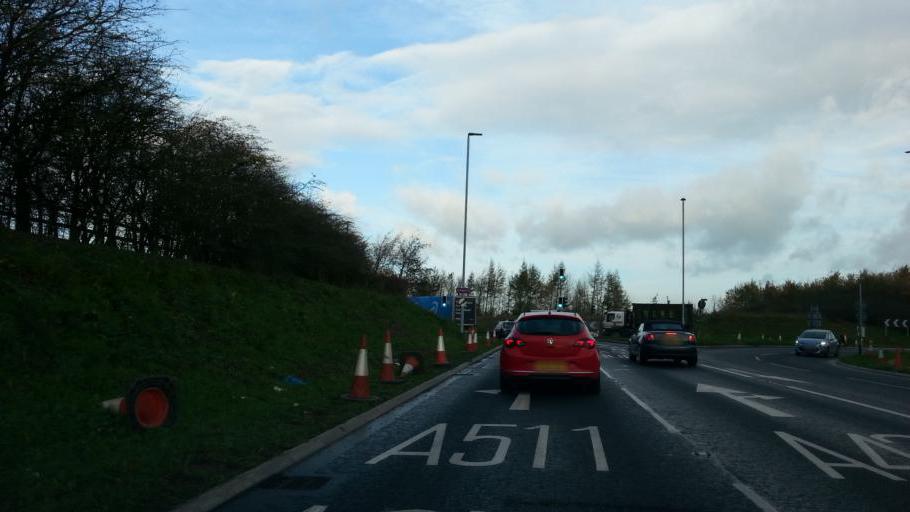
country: GB
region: England
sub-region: Leicestershire
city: Ashby de la Zouch
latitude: 52.7481
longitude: -1.4456
